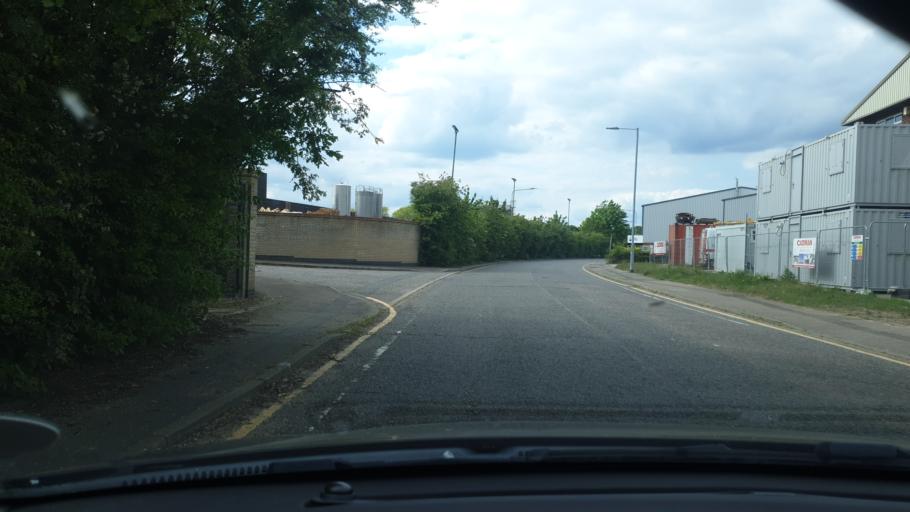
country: GB
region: England
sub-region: Essex
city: Colchester
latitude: 51.9195
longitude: 0.9233
